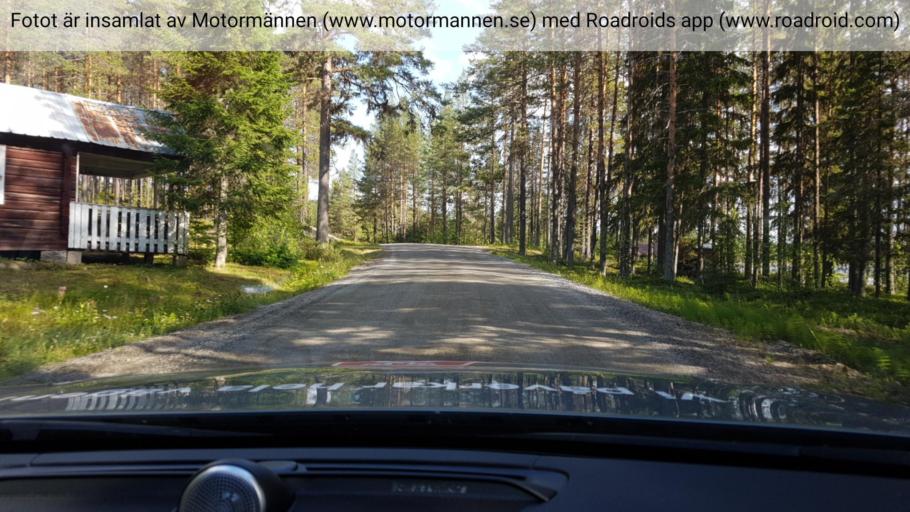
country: SE
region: Vaesterbotten
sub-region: Dorotea Kommun
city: Dorotea
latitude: 63.9744
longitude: 16.0533
